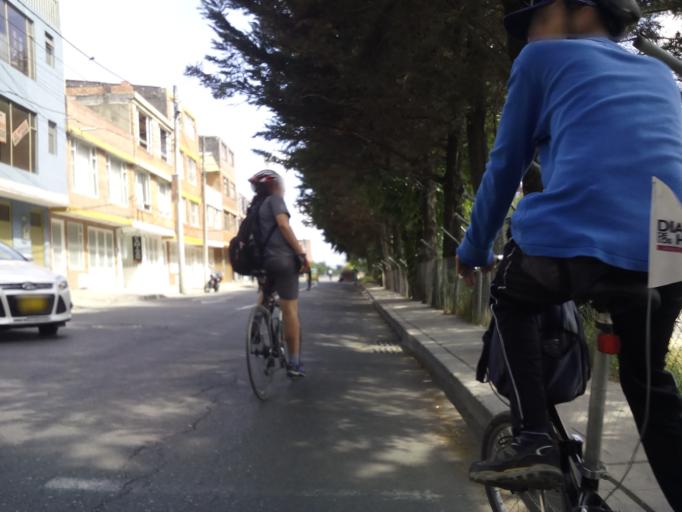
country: CO
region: Bogota D.C.
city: Bogota
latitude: 4.6724
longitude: -74.1362
